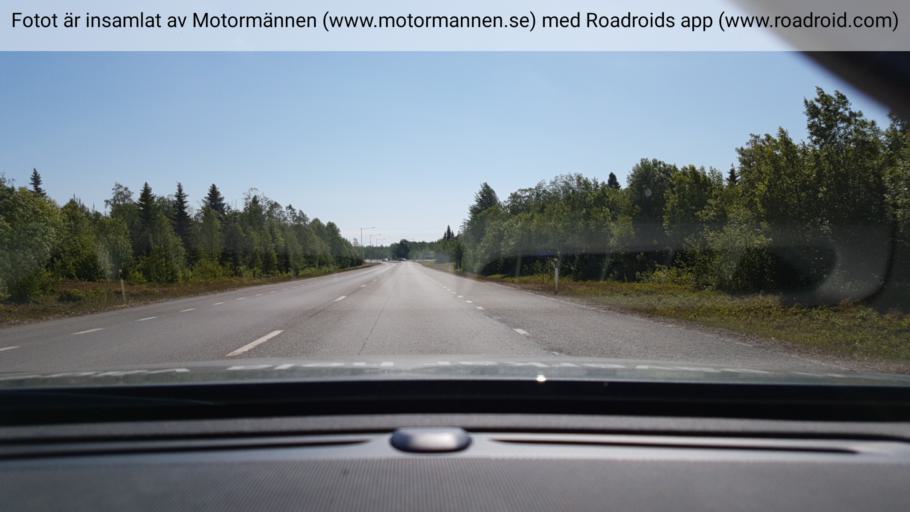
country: SE
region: Vaesterbotten
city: Obbola
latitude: 63.7122
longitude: 20.3169
